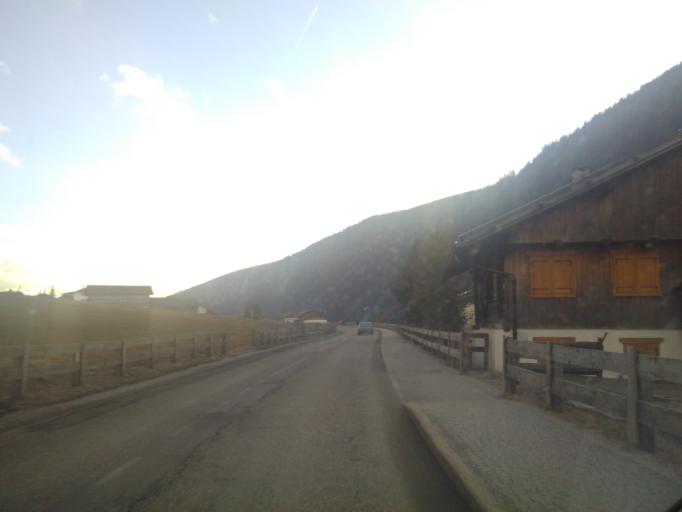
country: IT
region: Trentino-Alto Adige
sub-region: Bolzano
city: Fortezza
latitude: 46.8465
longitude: 11.6232
